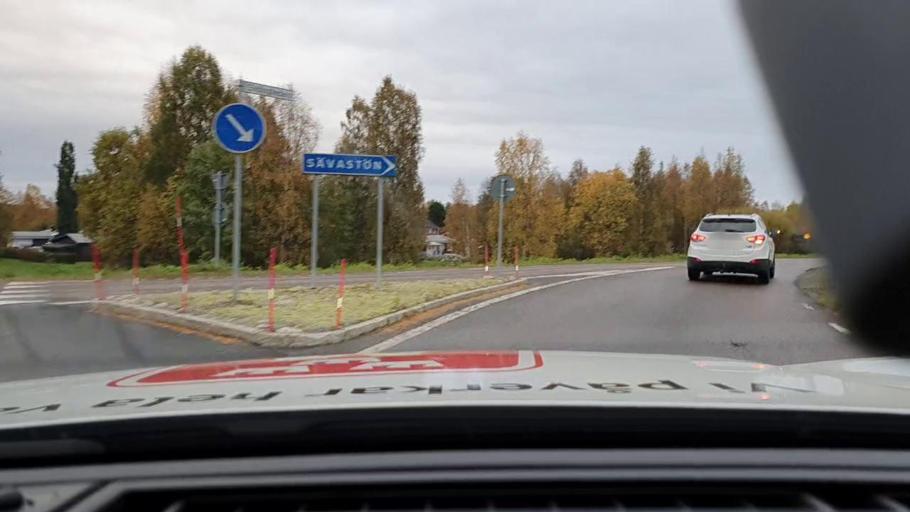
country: SE
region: Norrbotten
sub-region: Bodens Kommun
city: Saevast
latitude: 65.7681
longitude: 21.7400
